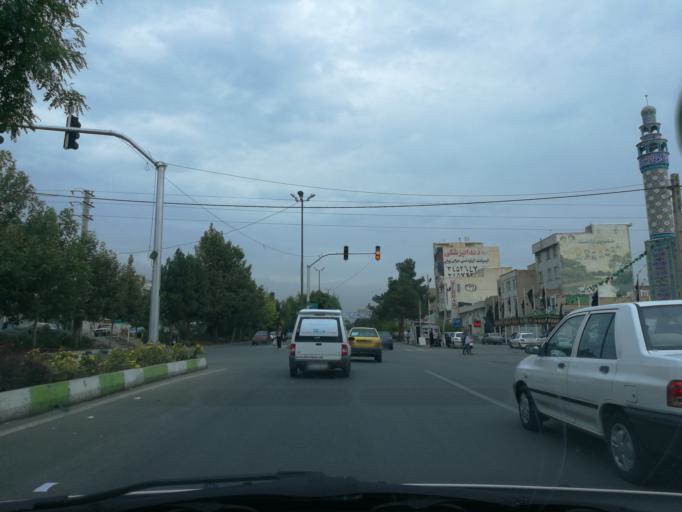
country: IR
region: Alborz
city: Karaj
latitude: 35.8590
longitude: 50.9449
